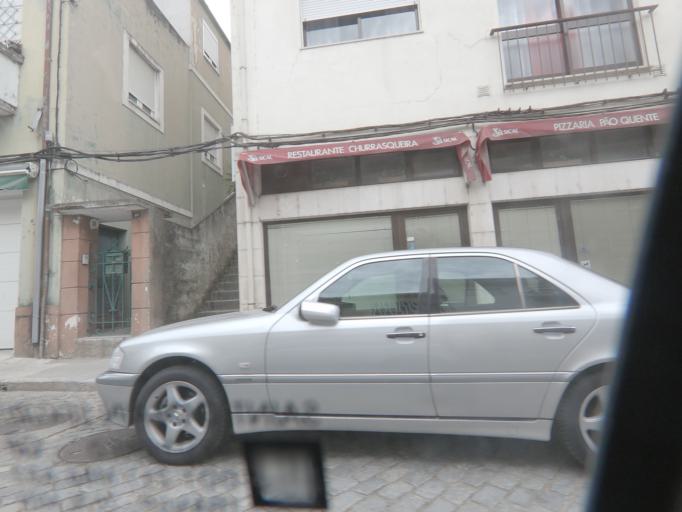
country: PT
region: Vila Real
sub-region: Sabrosa
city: Vilela
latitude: 41.1919
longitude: -7.5480
